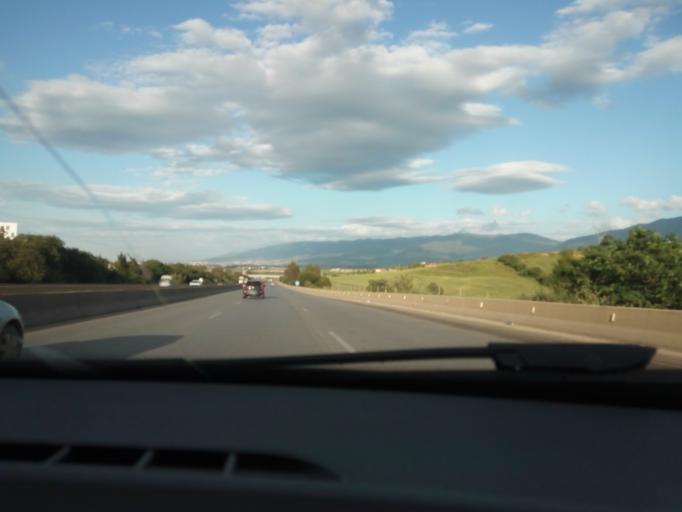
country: DZ
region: Tipaza
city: El Affroun
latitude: 36.4458
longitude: 2.6306
